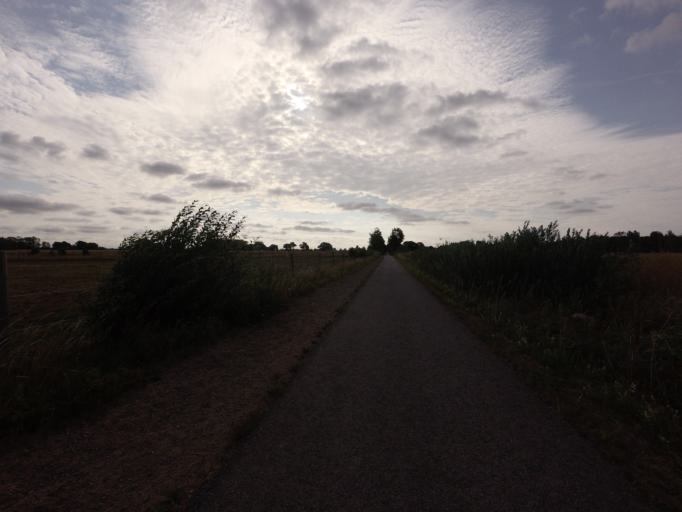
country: SE
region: Skane
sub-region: Hoganas Kommun
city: Hoganas
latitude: 56.1827
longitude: 12.6515
